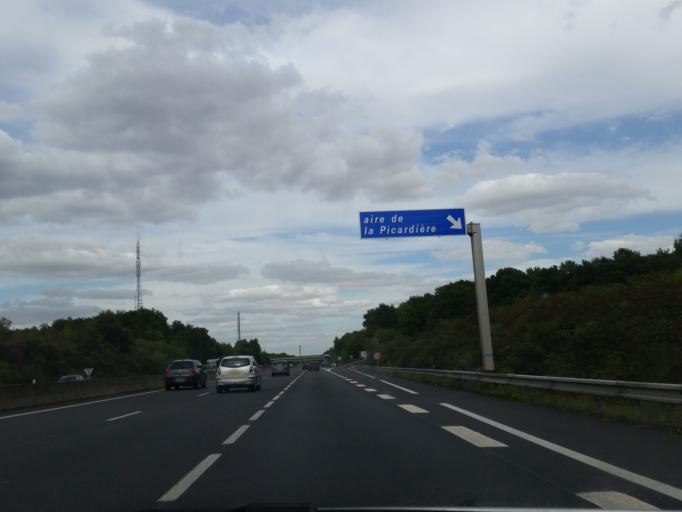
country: FR
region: Centre
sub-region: Departement d'Indre-et-Loire
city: Auzouer-en-Touraine
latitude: 47.5337
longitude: 0.9581
